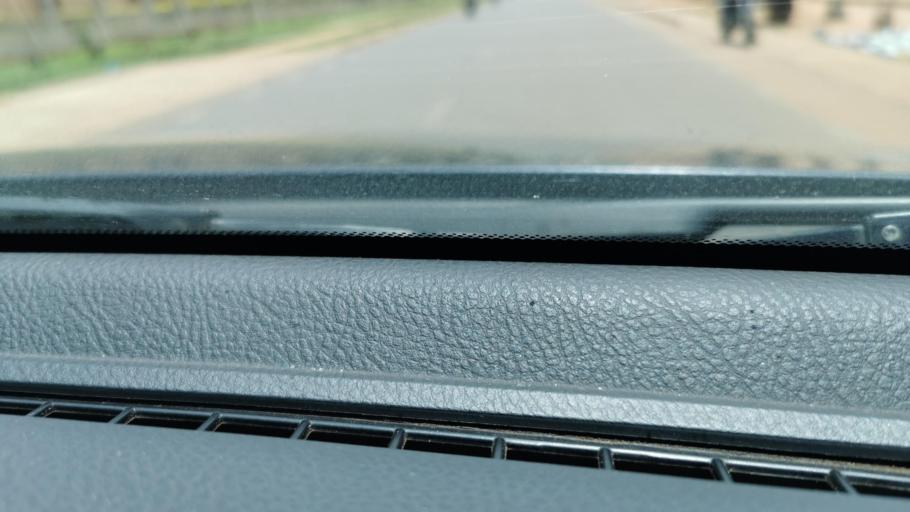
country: TG
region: Maritime
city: Lome
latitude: 6.2096
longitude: 1.1958
